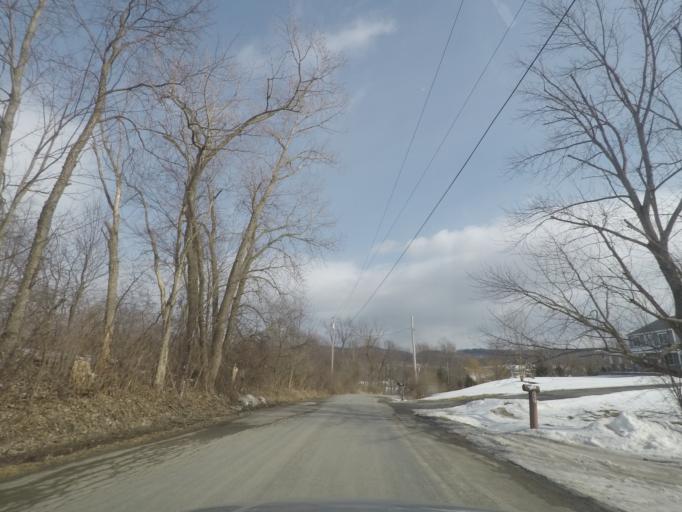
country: US
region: New York
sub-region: Rensselaer County
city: Poestenkill
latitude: 42.7844
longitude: -73.5616
